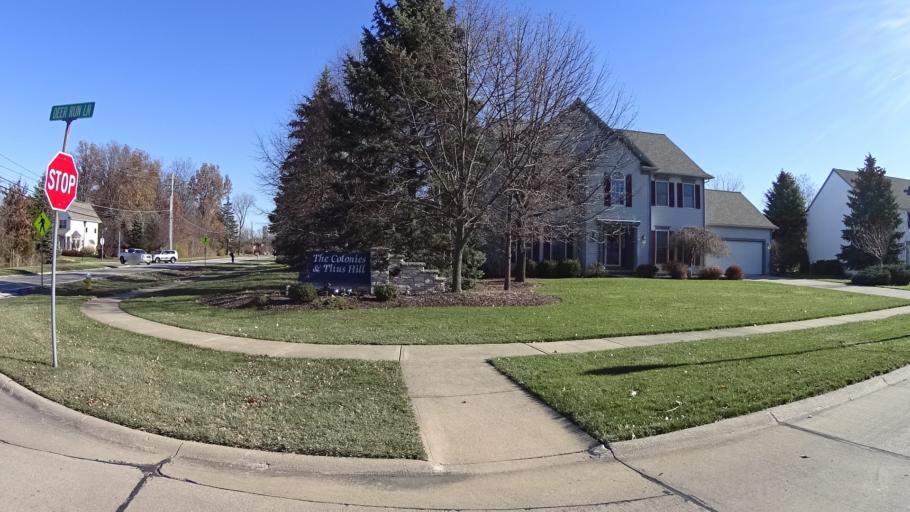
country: US
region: Ohio
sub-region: Lorain County
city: Avon Lake
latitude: 41.4883
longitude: -82.0231
